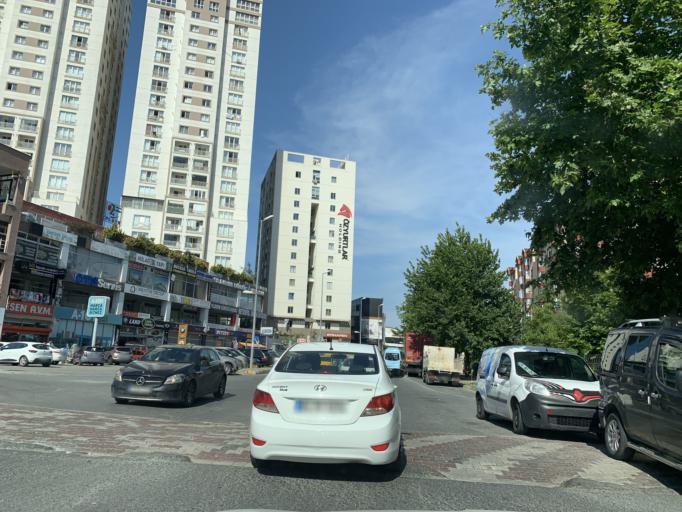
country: TR
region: Istanbul
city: Esenyurt
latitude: 41.0648
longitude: 28.6692
